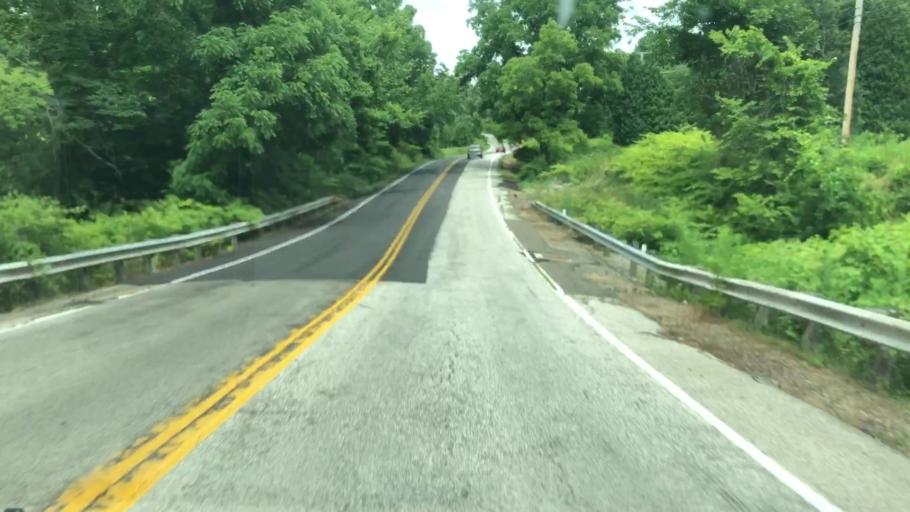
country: US
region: Ohio
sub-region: Summit County
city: Peninsula
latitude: 41.1760
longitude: -81.5605
